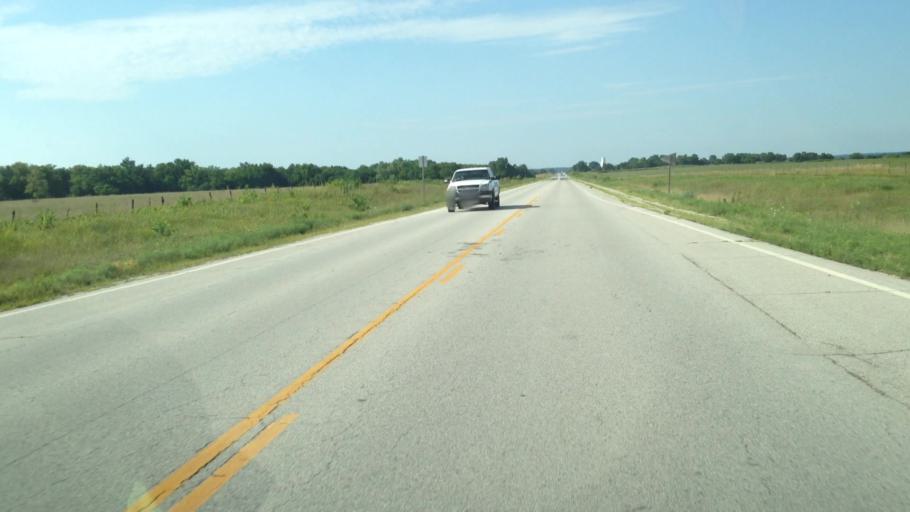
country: US
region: Kansas
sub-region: Neosho County
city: Erie
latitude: 37.4864
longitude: -95.2692
